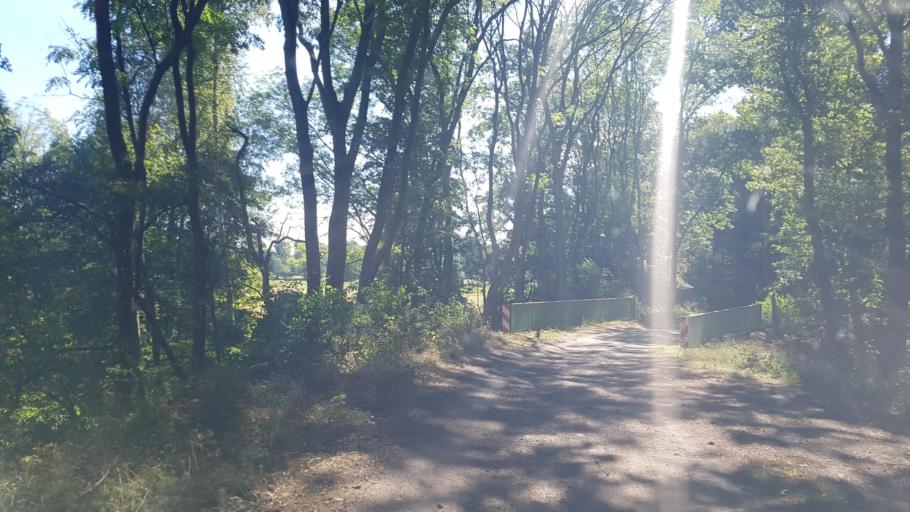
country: DE
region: Brandenburg
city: Brandenburg an der Havel
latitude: 52.3449
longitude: 12.5291
